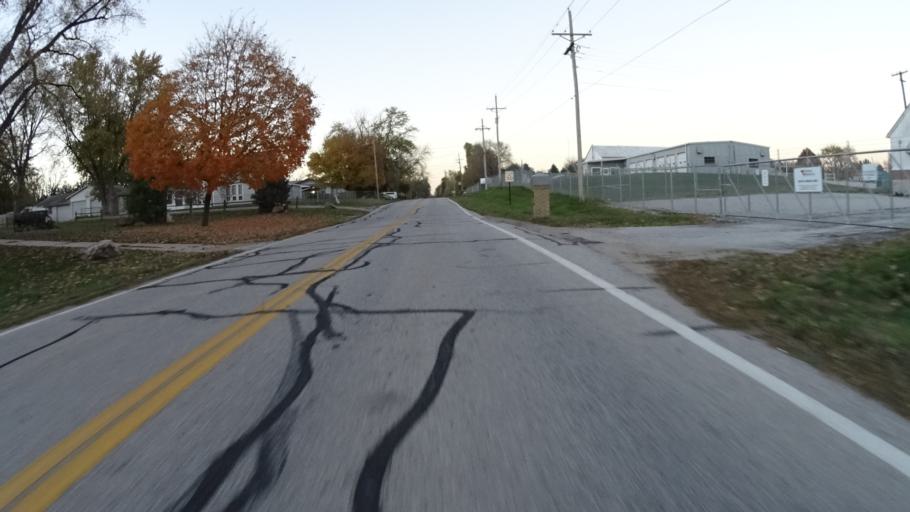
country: US
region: Nebraska
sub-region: Sarpy County
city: Offutt Air Force Base
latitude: 41.1749
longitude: -95.9527
